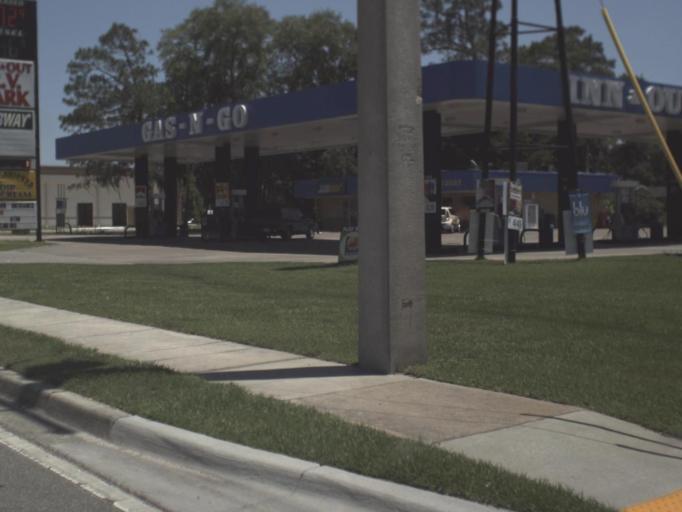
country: US
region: Florida
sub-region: Columbia County
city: Lake City
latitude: 30.1802
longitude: -82.6822
